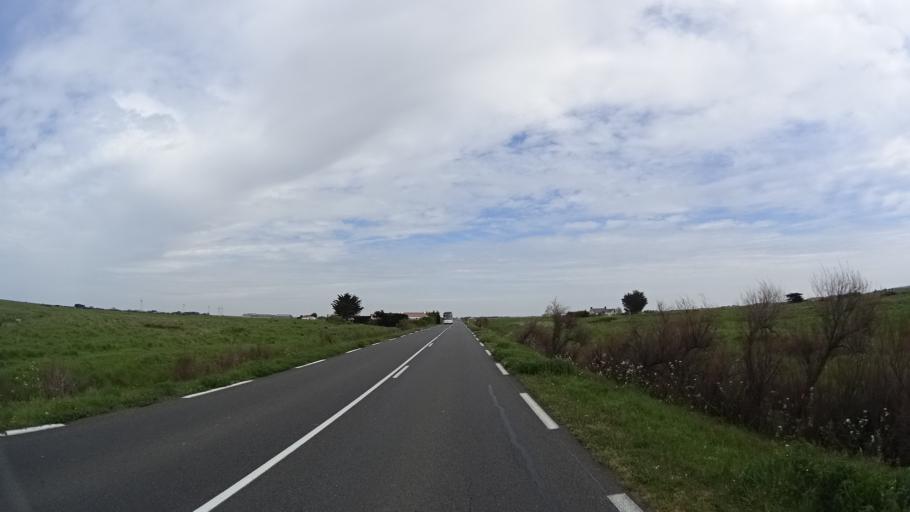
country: FR
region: Pays de la Loire
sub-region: Departement de la Vendee
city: Beauvoir-sur-Mer
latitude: 46.9284
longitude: -2.0399
